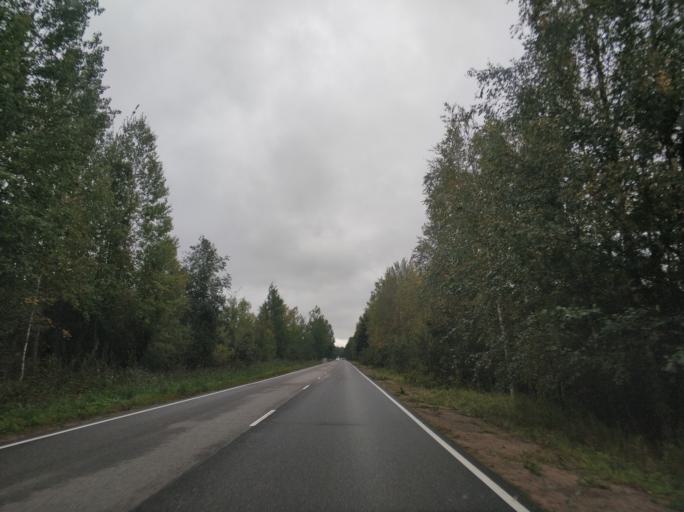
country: RU
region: Leningrad
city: Borisova Griva
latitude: 60.1407
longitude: 30.9515
